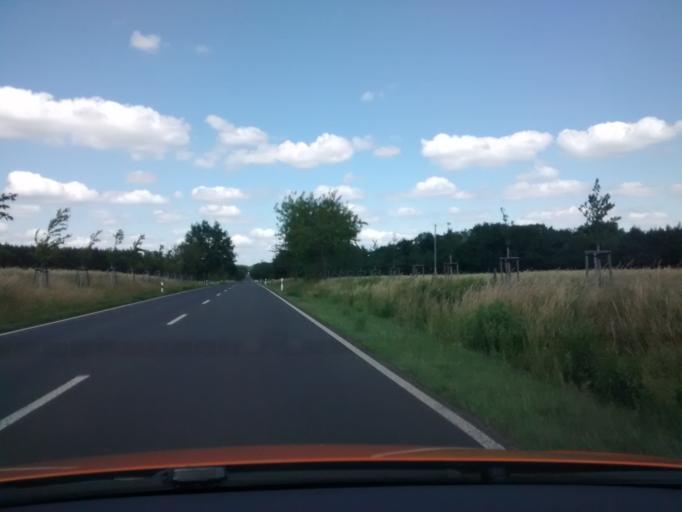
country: DE
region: Berlin
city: Kladow
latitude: 52.4807
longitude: 13.1084
